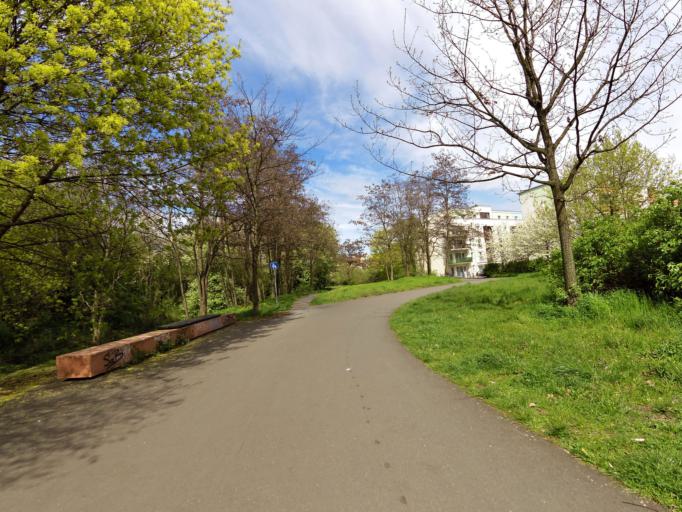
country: DE
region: Berlin
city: Baumschulenweg
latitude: 52.4629
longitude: 13.4782
